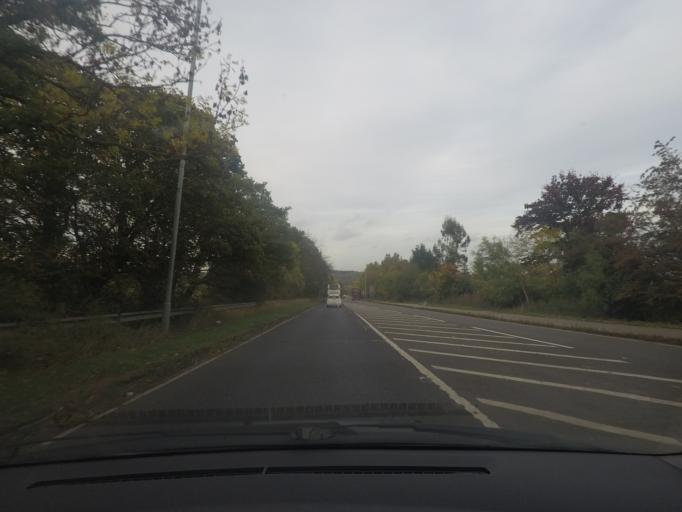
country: GB
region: England
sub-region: Barnsley
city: Wortley
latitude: 53.4723
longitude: -1.5049
